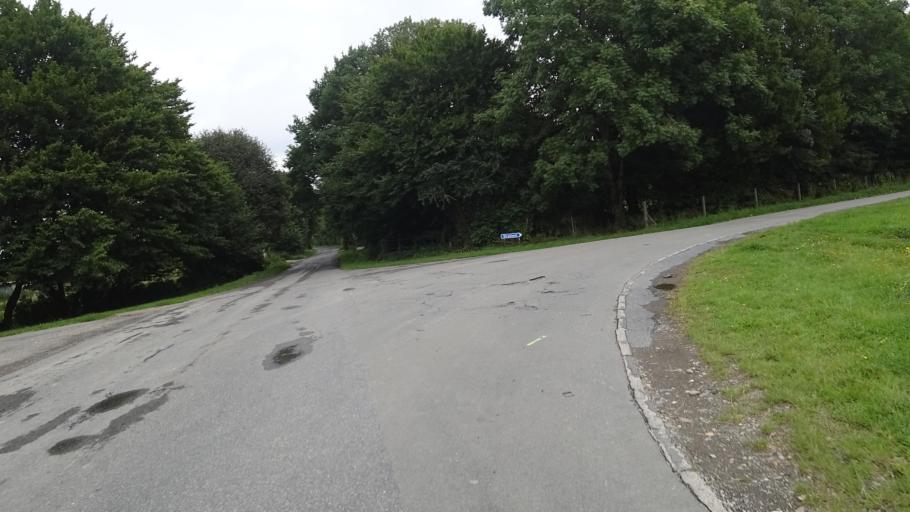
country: BE
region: Wallonia
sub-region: Province du Luxembourg
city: Chiny
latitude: 49.8061
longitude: 5.3631
